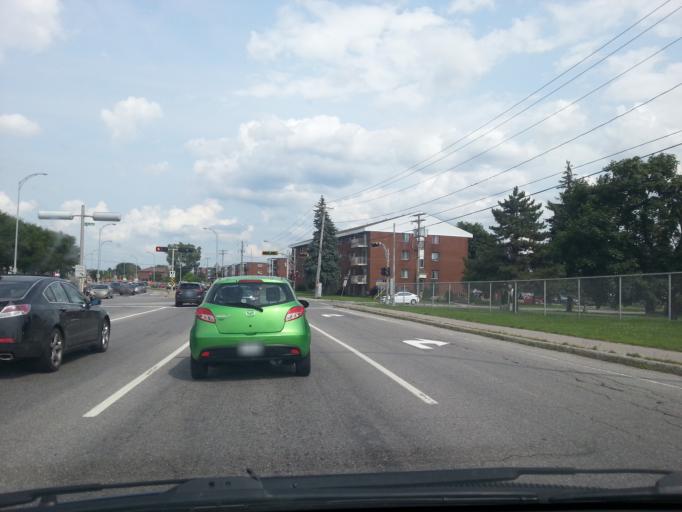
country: CA
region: Quebec
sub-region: Outaouais
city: Gatineau
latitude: 45.4879
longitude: -75.7130
